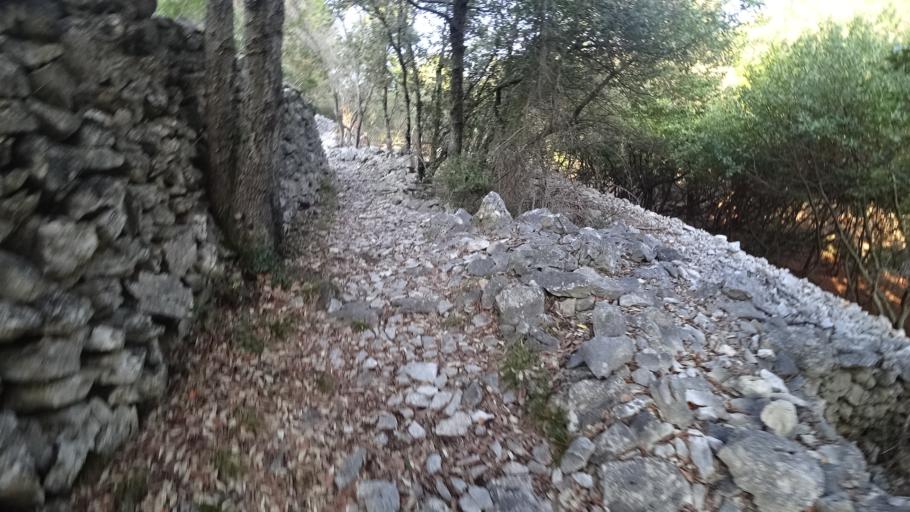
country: HR
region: Primorsko-Goranska
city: Mali Losinj
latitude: 44.5160
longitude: 14.4765
